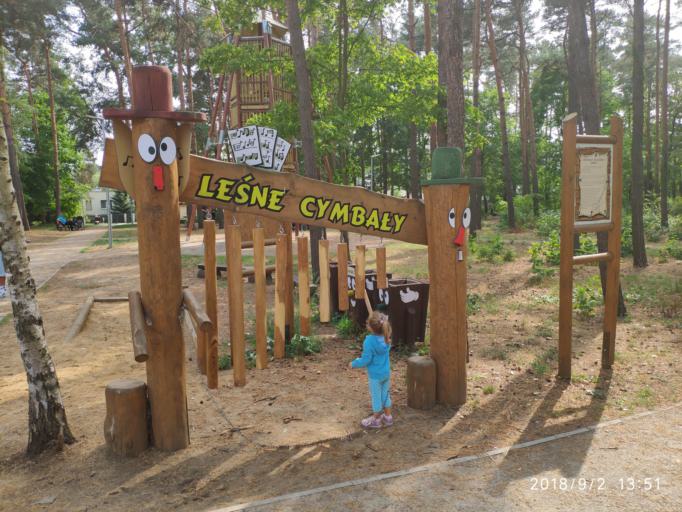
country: PL
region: Lubusz
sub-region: Zielona Gora
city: Zielona Gora
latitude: 51.9243
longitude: 15.5165
